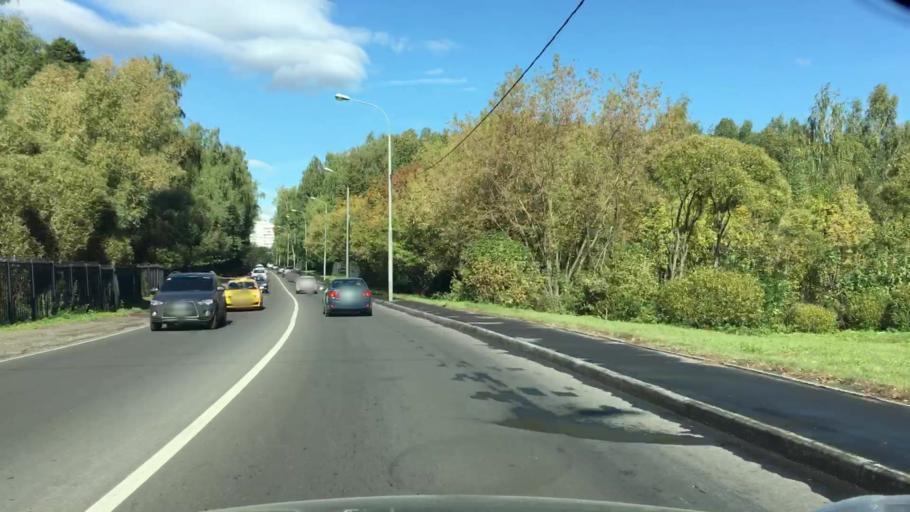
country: RU
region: Moskovskaya
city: Izmaylovo
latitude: 55.7837
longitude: 37.8207
